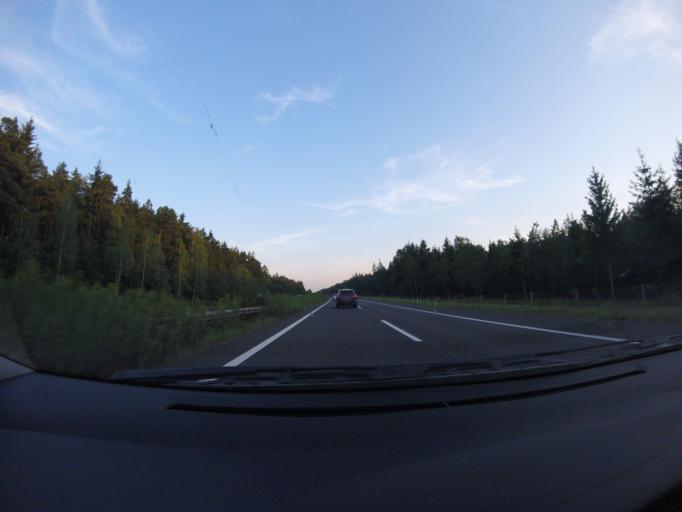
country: AT
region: Styria
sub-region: Politischer Bezirk Hartberg-Fuerstenfeld
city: Bad Waltersdorf
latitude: 47.1310
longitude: 15.9854
